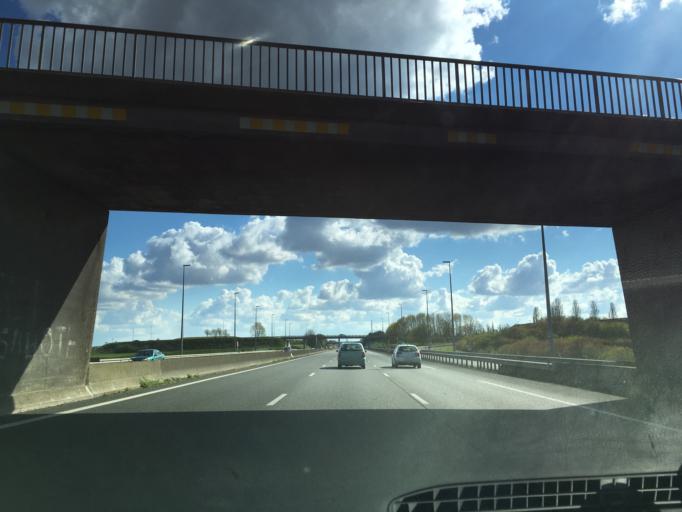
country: FR
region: Nord-Pas-de-Calais
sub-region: Departement du Pas-de-Calais
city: Fampoux
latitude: 50.2731
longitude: 2.8706
